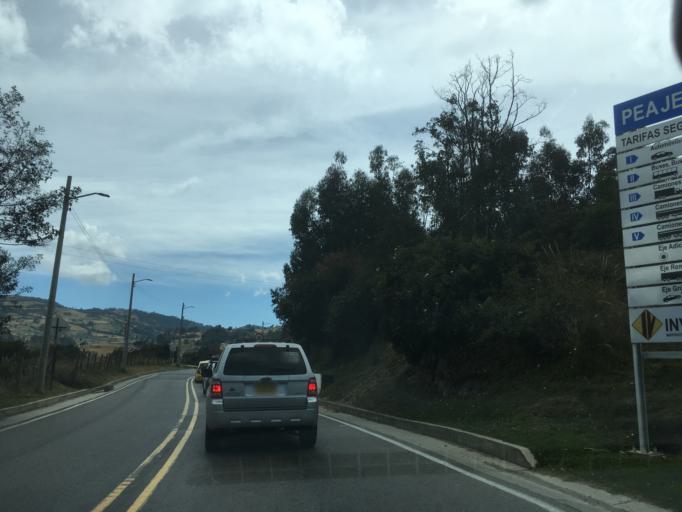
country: CO
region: Boyaca
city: Firavitoba
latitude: 5.6329
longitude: -72.9219
